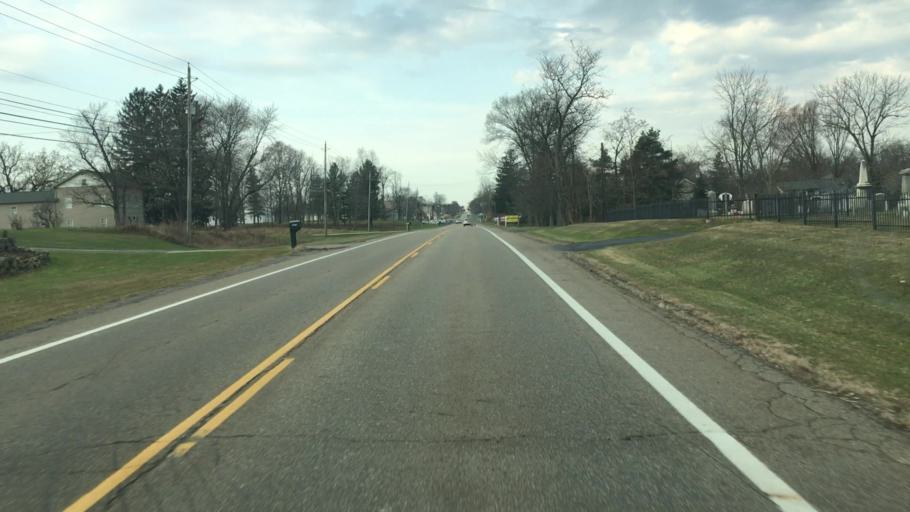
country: US
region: Ohio
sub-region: Mahoning County
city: Canfield
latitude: 41.0244
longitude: -80.8508
